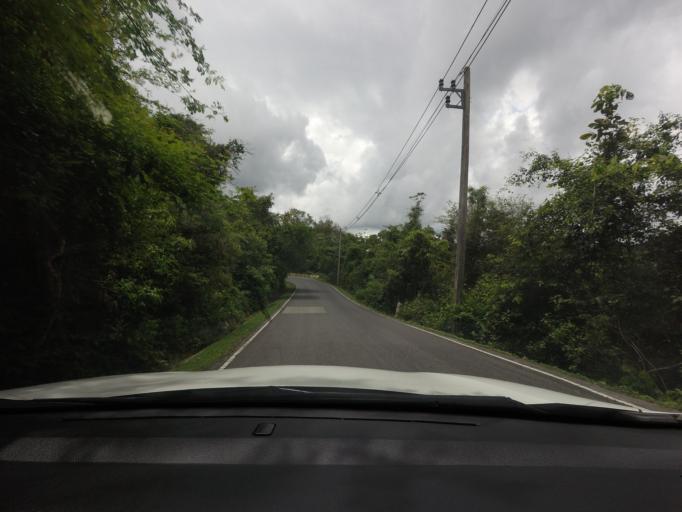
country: TH
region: Nakhon Ratchasima
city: Pak Chong
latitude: 14.4720
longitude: 101.3929
